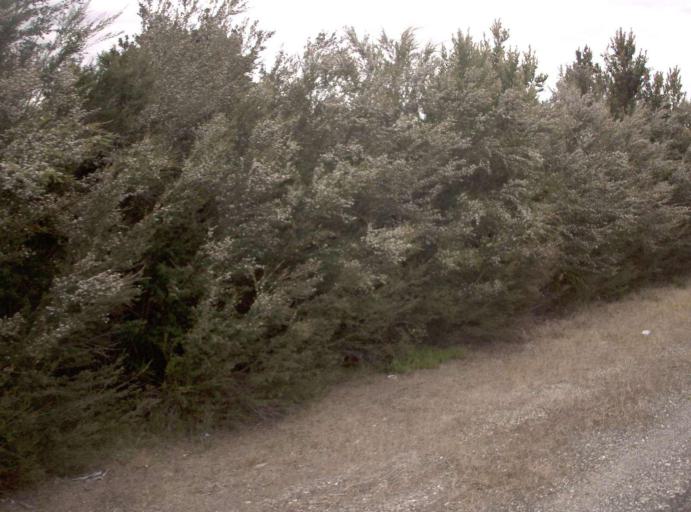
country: AU
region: Victoria
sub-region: Wellington
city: Sale
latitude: -38.1923
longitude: 147.3658
